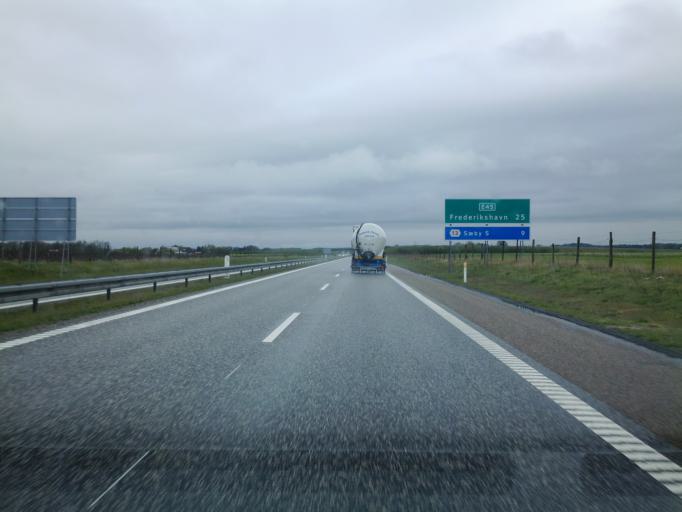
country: DK
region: North Denmark
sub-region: Bronderslev Kommune
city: Dronninglund
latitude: 57.2544
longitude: 10.3454
